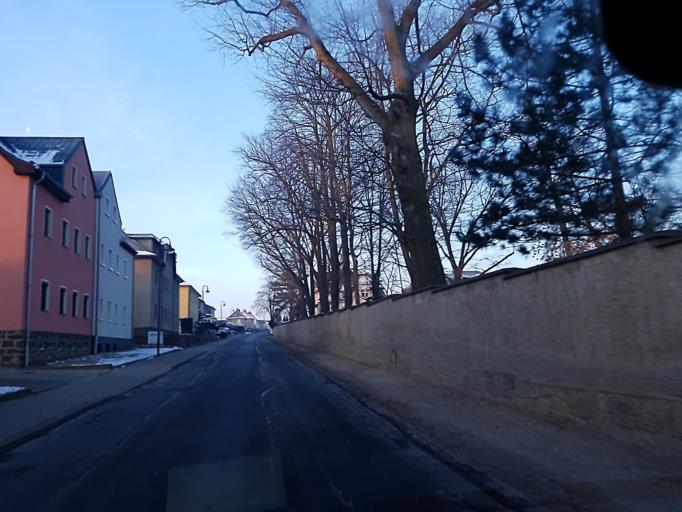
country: DE
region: Saxony
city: Mugeln
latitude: 51.2334
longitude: 13.0390
